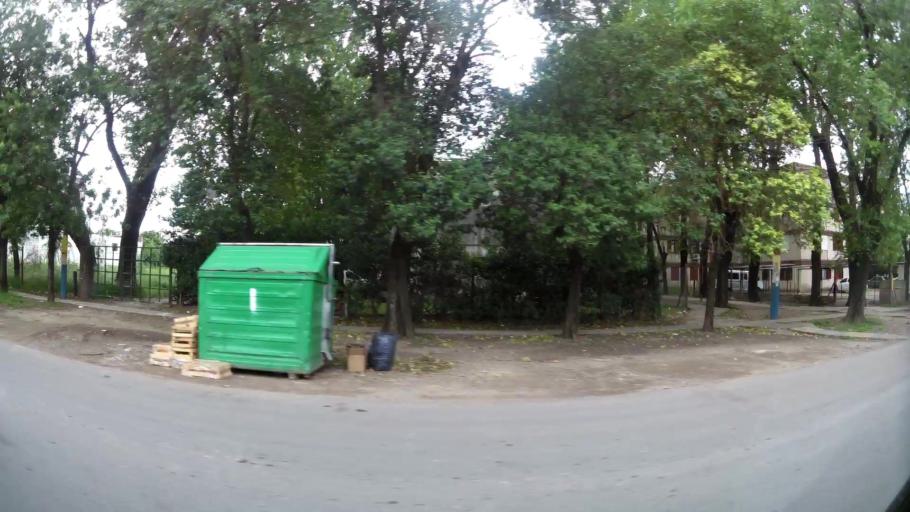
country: AR
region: Santa Fe
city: Gobernador Galvez
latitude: -32.9975
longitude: -60.6609
